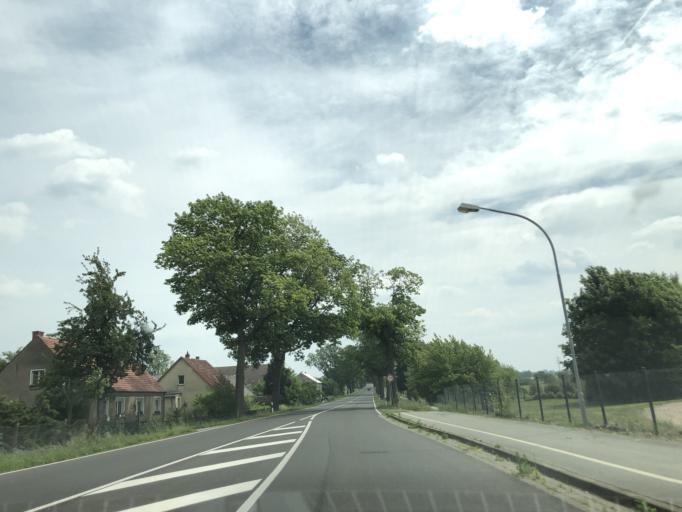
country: DE
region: Brandenburg
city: Kyritz
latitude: 52.9619
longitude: 12.3391
